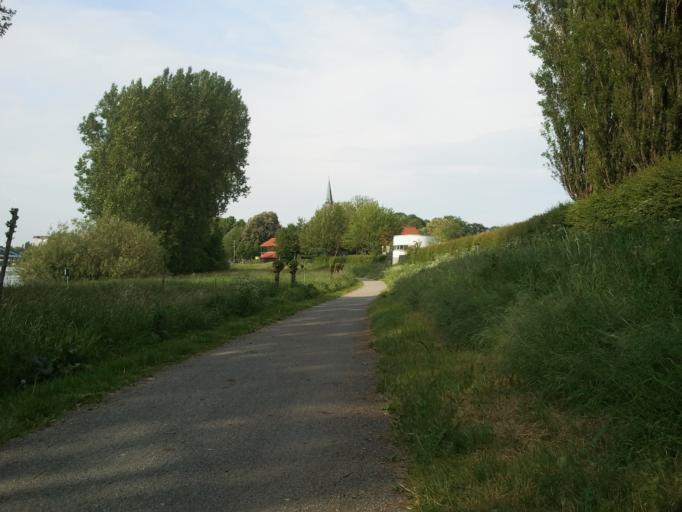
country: DE
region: Lower Saxony
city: Nienburg
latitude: 52.6336
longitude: 9.2046
